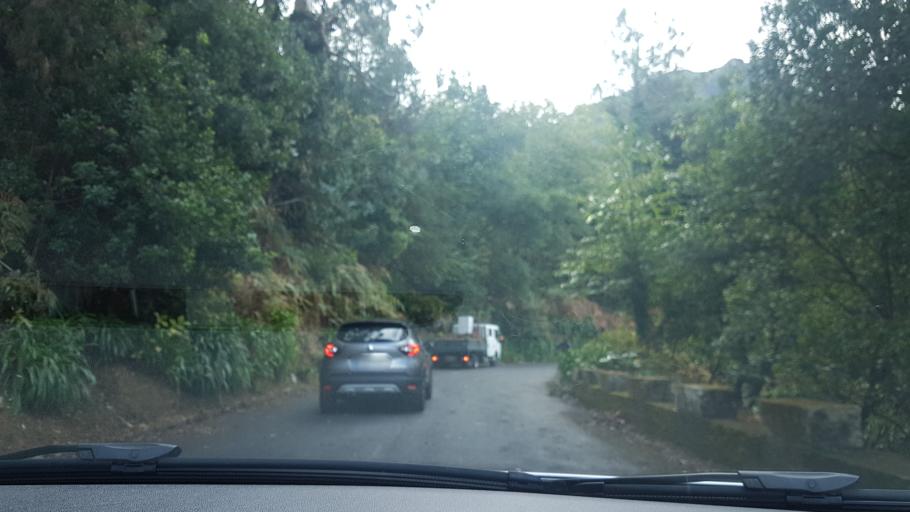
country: PT
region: Madeira
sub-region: Sao Vicente
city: Sao Vicente
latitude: 32.7702
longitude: -17.0272
